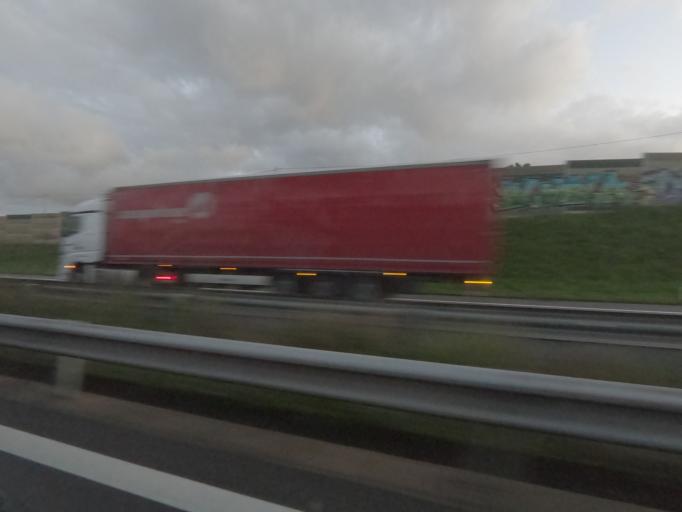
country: PT
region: Porto
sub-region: Paredes
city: Casteloes de Cepeda
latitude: 41.1988
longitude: -8.3443
